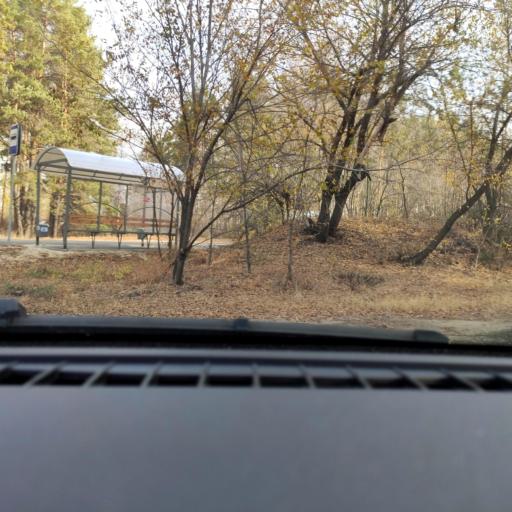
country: RU
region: Voronezj
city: Maslovka
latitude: 51.5773
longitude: 39.2959
